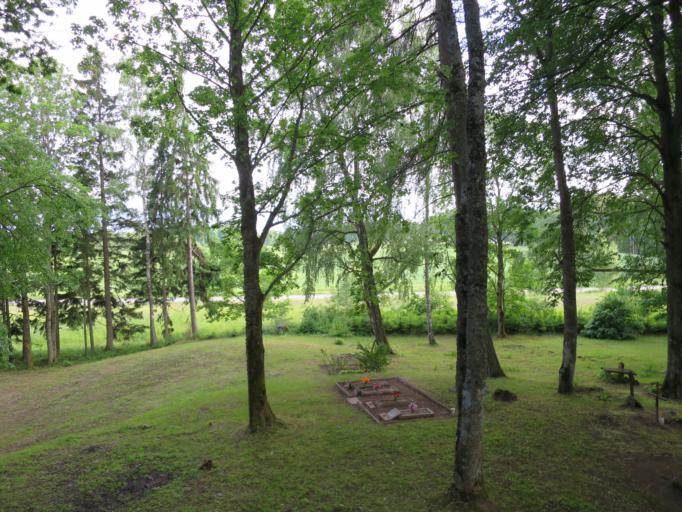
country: LV
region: Skrunda
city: Skrunda
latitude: 56.6911
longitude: 21.8753
